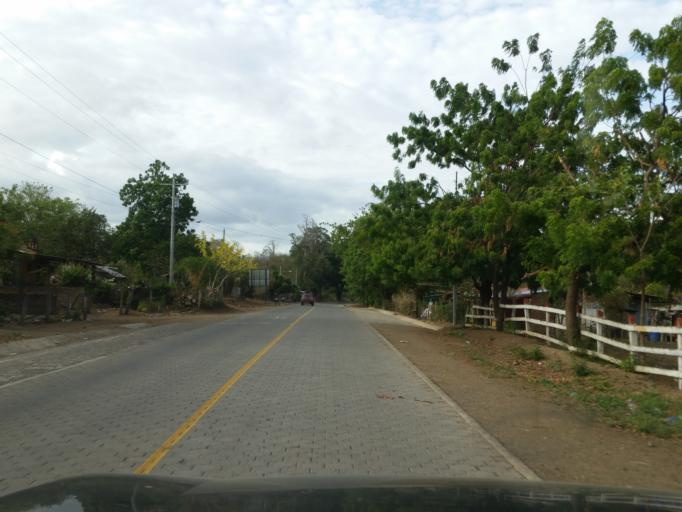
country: NI
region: Rivas
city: Tola
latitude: 11.4177
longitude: -85.9490
